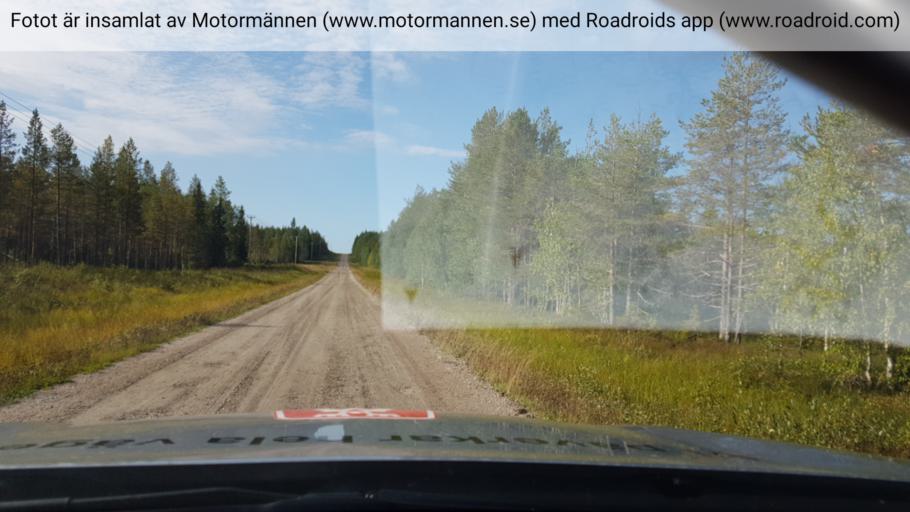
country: FI
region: Lapland
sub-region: Torniolaakso
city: Ylitornio
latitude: 66.1984
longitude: 23.4222
